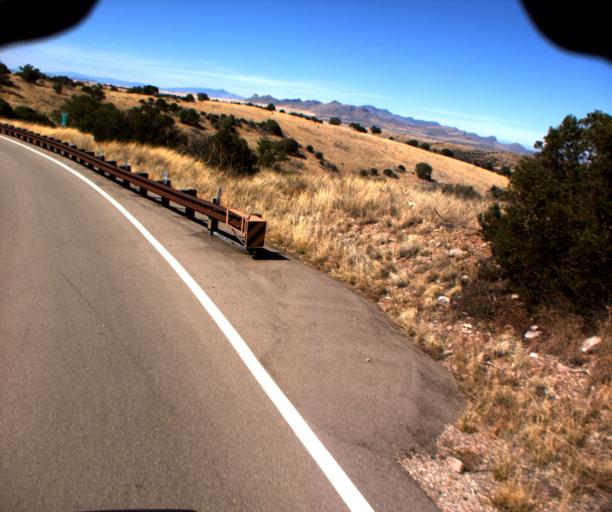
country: US
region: Arizona
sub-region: Cochise County
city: Huachuca City
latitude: 31.5222
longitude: -110.4993
